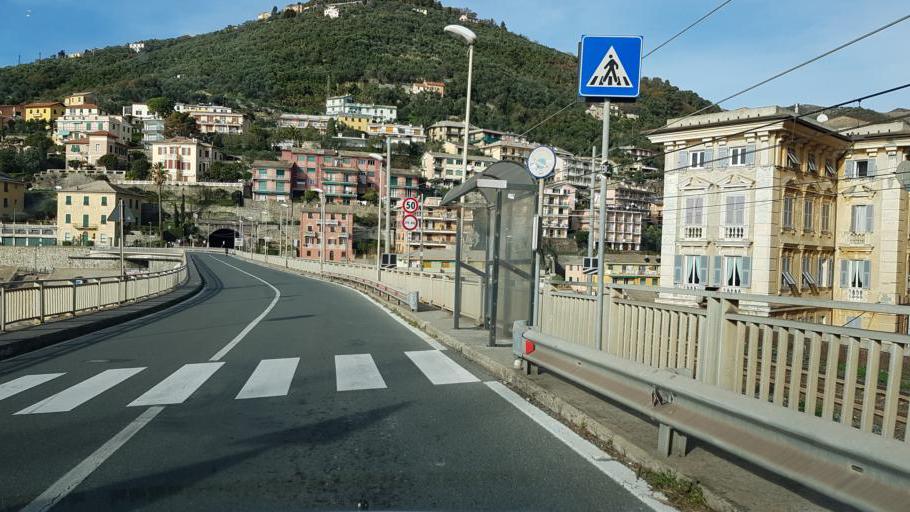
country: IT
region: Liguria
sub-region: Provincia di Genova
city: Sori
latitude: 44.3714
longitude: 9.1045
